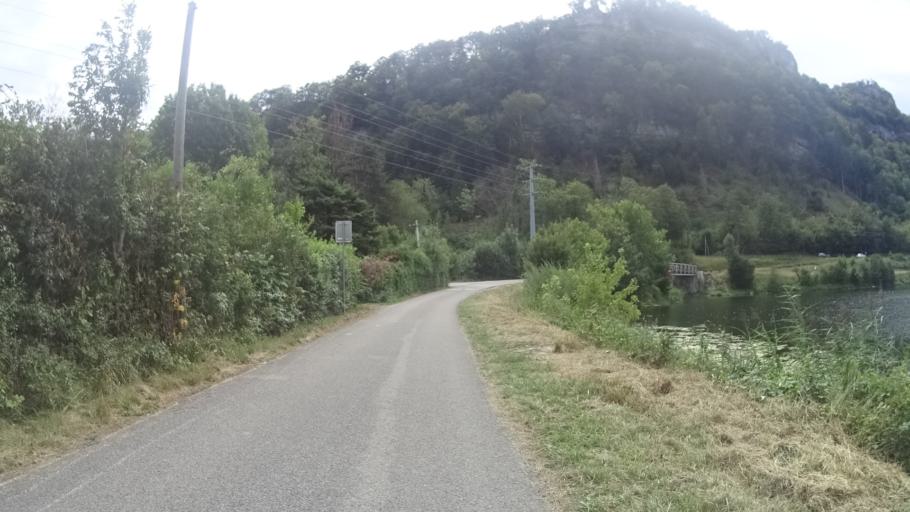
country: FR
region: Franche-Comte
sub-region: Departement du Doubs
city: Baume-les-Dames
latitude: 47.3422
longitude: 6.3738
